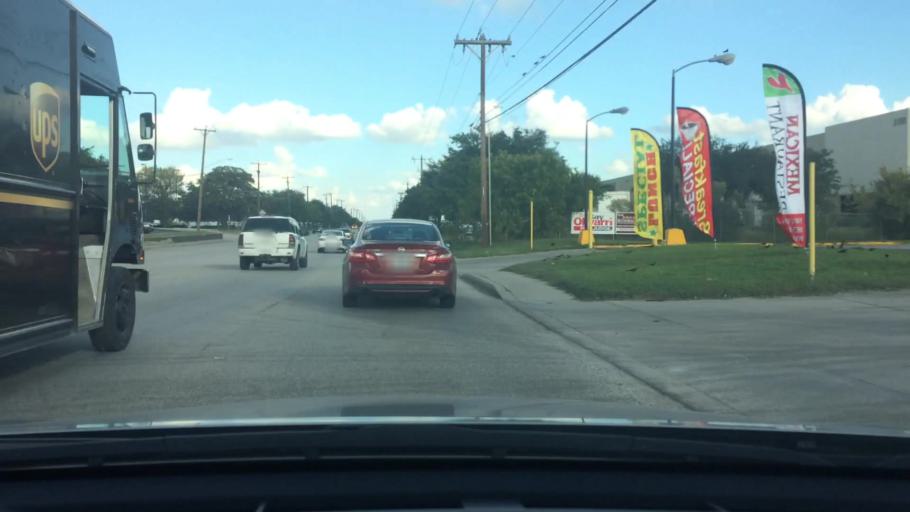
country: US
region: Texas
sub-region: Bexar County
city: Kirby
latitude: 29.4840
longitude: -98.3915
